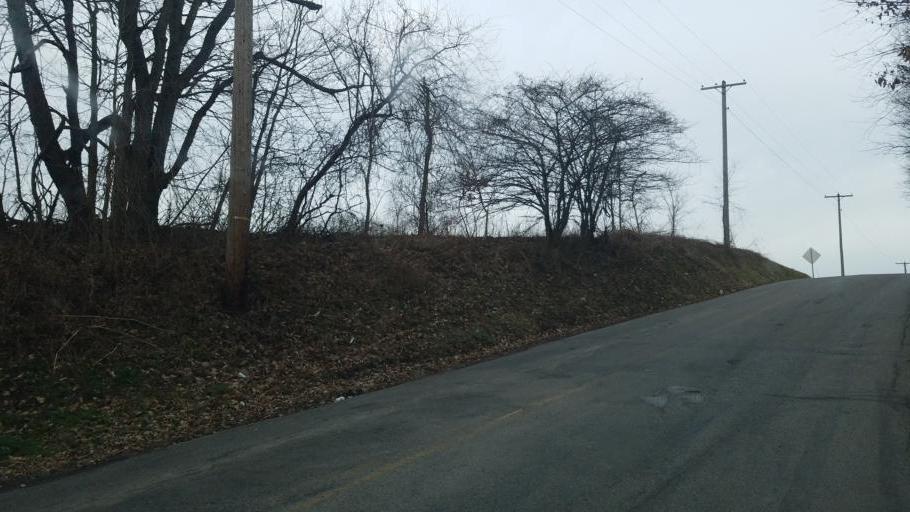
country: US
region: Ohio
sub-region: Richland County
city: Lincoln Heights
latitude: 40.7431
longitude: -82.4553
